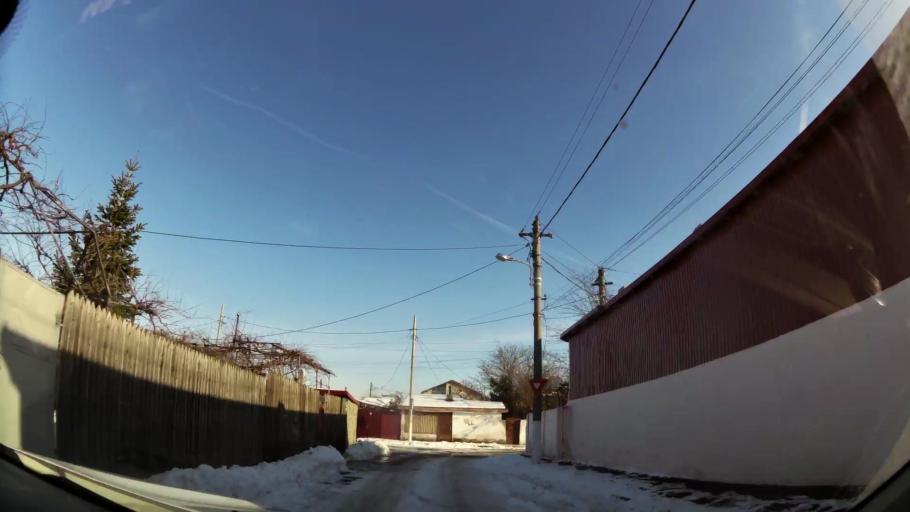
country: RO
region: Ilfov
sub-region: Voluntari City
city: Voluntari
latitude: 44.4836
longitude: 26.1426
